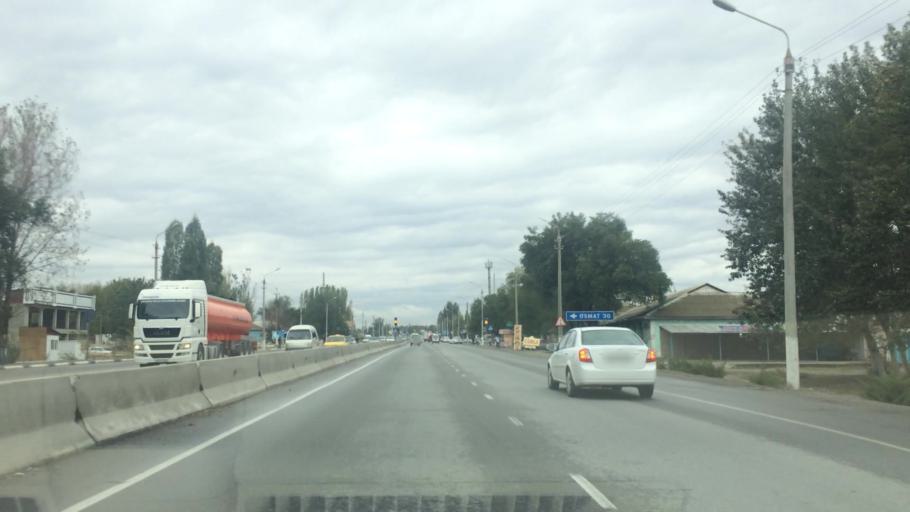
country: UZ
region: Jizzax
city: Jizzax
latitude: 39.9843
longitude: 67.5741
